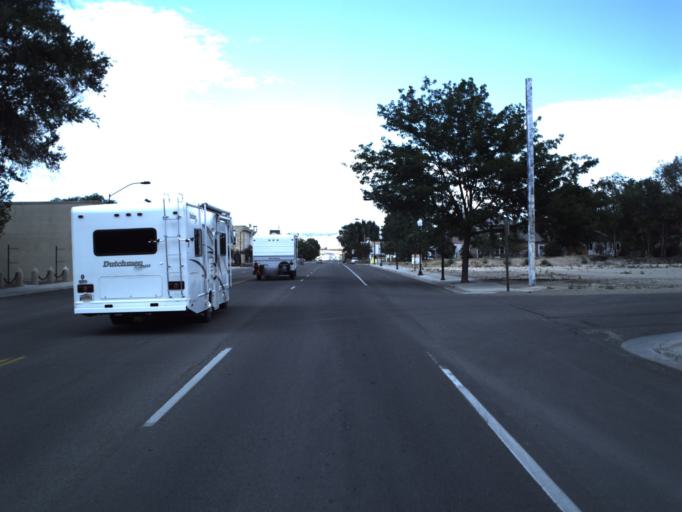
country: US
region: Utah
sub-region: Sanpete County
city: Gunnison
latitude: 39.1519
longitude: -111.8183
